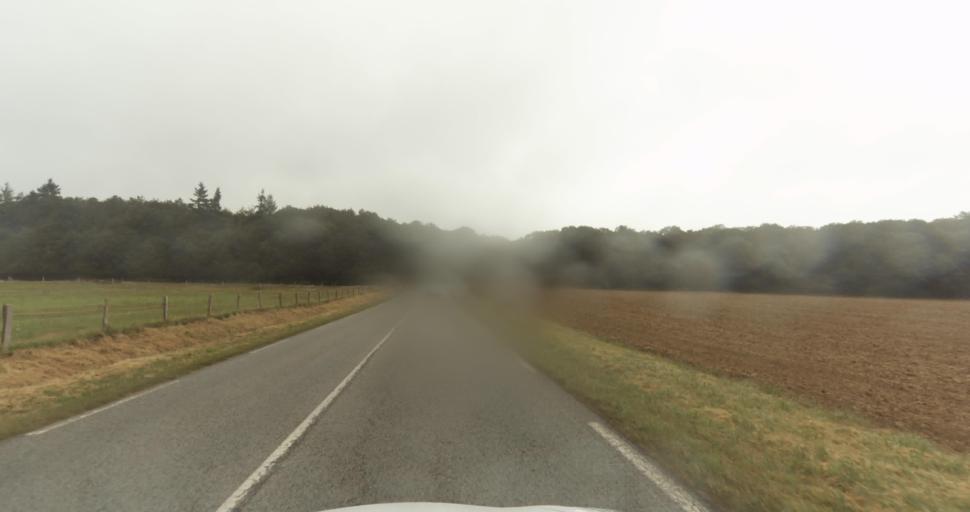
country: FR
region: Haute-Normandie
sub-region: Departement de l'Eure
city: Heudreville-sur-Eure
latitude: 49.1113
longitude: 1.1738
